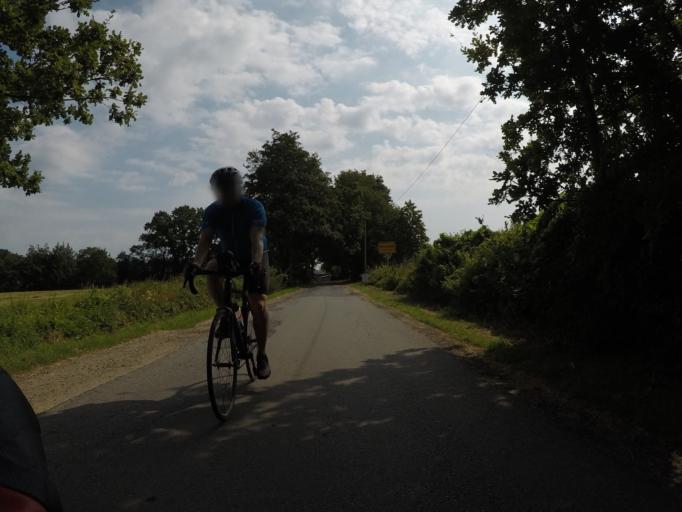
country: DE
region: Schleswig-Holstein
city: Tangstedt
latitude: 53.7532
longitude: 10.0588
